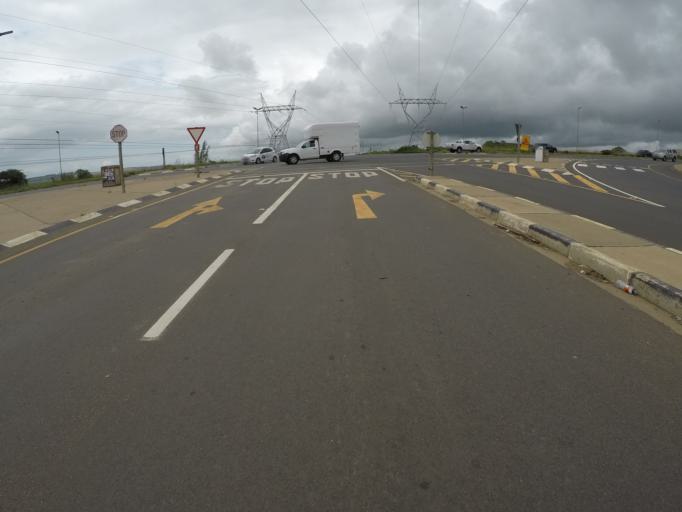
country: ZA
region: KwaZulu-Natal
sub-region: uThungulu District Municipality
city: Empangeni
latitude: -28.7703
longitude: 31.9382
